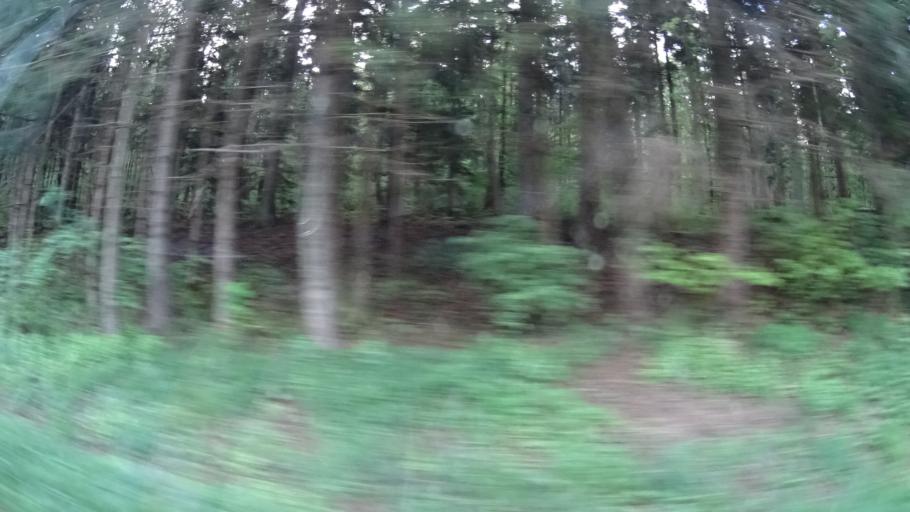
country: DE
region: Baden-Wuerttemberg
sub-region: Karlsruhe Region
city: Empfingen
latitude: 48.4288
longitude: 8.7659
